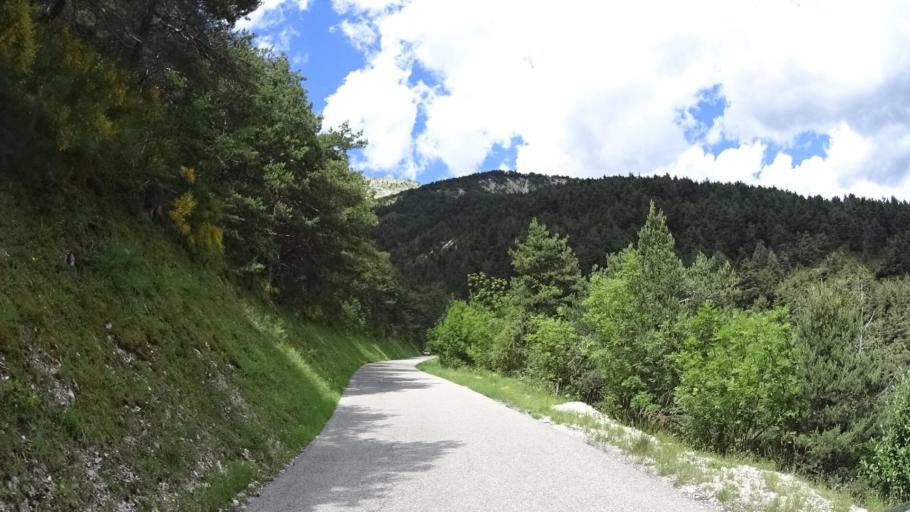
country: FR
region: Provence-Alpes-Cote d'Azur
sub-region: Departement des Alpes-de-Haute-Provence
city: Annot
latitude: 44.0205
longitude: 6.6210
